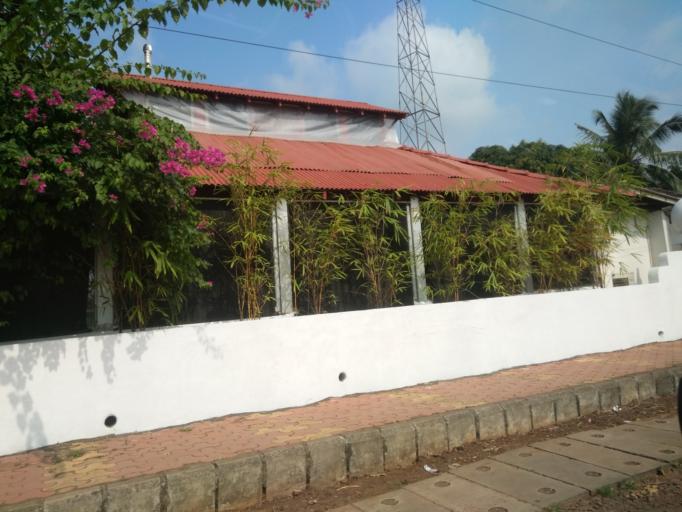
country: IN
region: Goa
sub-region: North Goa
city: Serula
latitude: 15.5359
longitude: 73.8204
